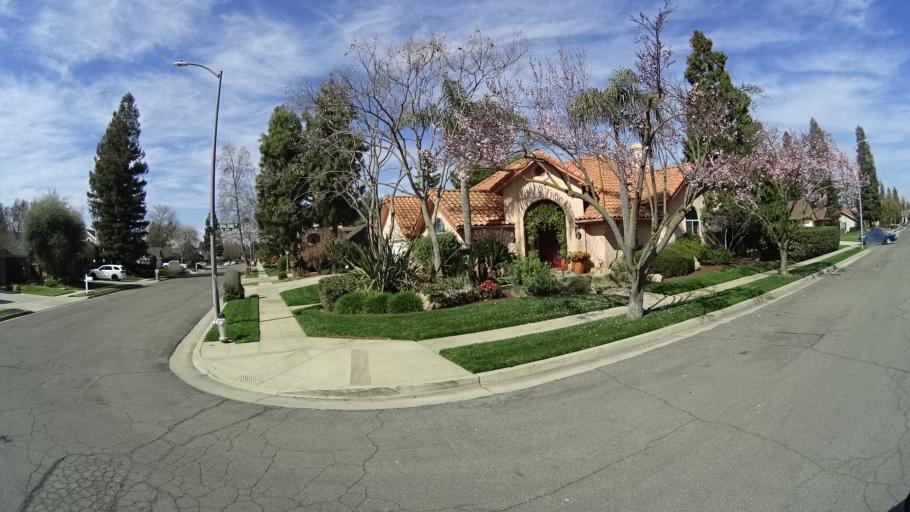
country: US
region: California
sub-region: Fresno County
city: Clovis
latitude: 36.8634
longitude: -119.7607
